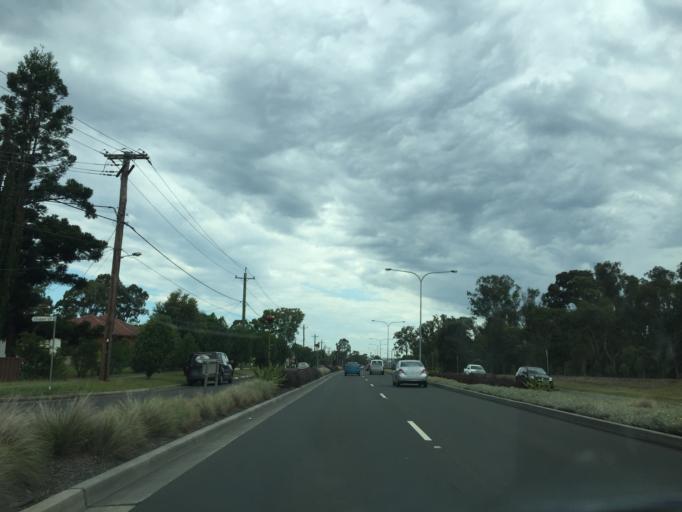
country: AU
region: New South Wales
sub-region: Blacktown
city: Doonside
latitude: -33.7588
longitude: 150.8641
